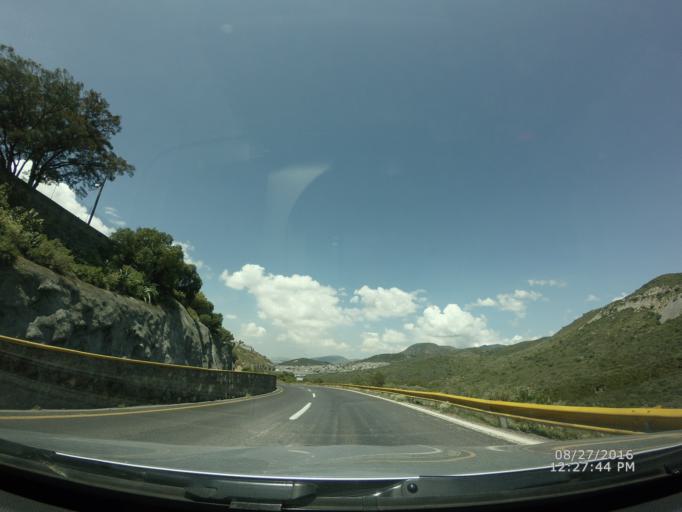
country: MX
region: Hidalgo
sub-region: Mineral de la Reforma
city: Colonia Militar
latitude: 20.1213
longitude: -98.6961
